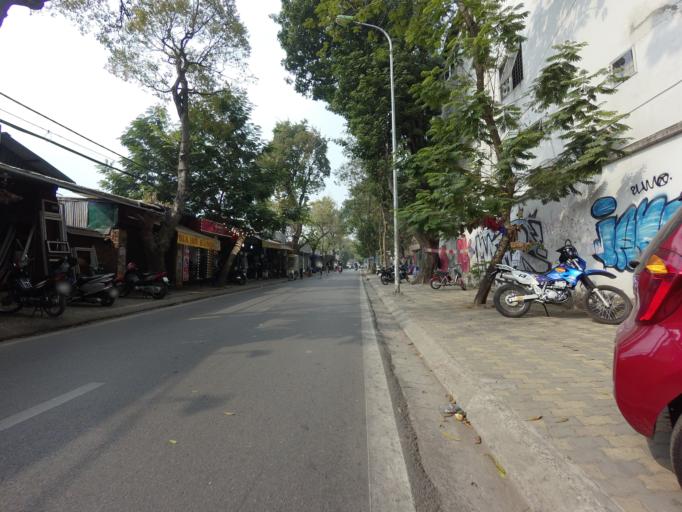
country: VN
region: Ha Noi
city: Tay Ho
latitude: 21.0557
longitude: 105.8351
